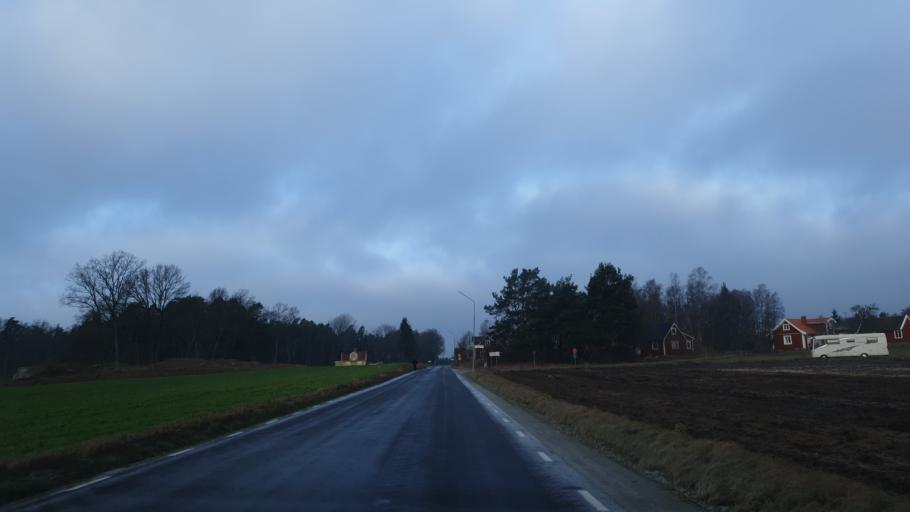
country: SE
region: Blekinge
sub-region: Karlshamns Kommun
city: Morrum
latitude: 56.1700
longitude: 14.7425
